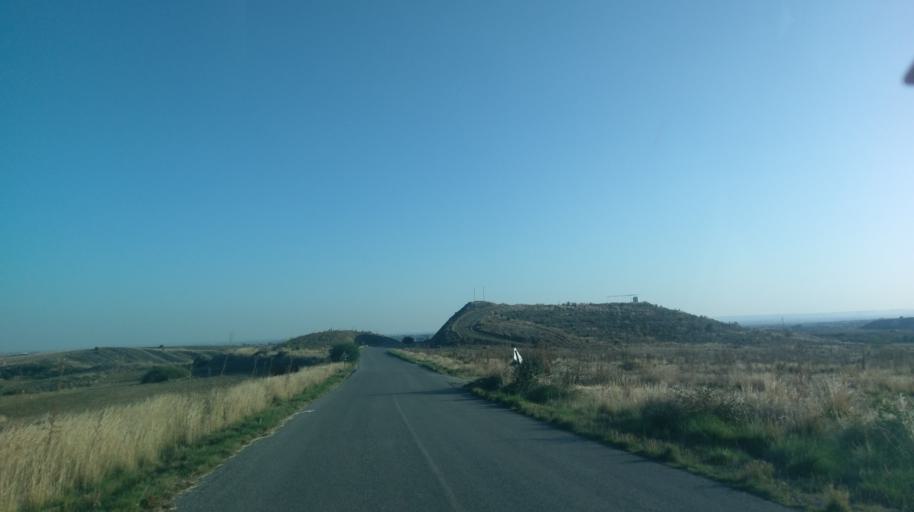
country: CY
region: Ammochostos
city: Lefkonoiko
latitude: 35.2840
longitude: 33.6571
